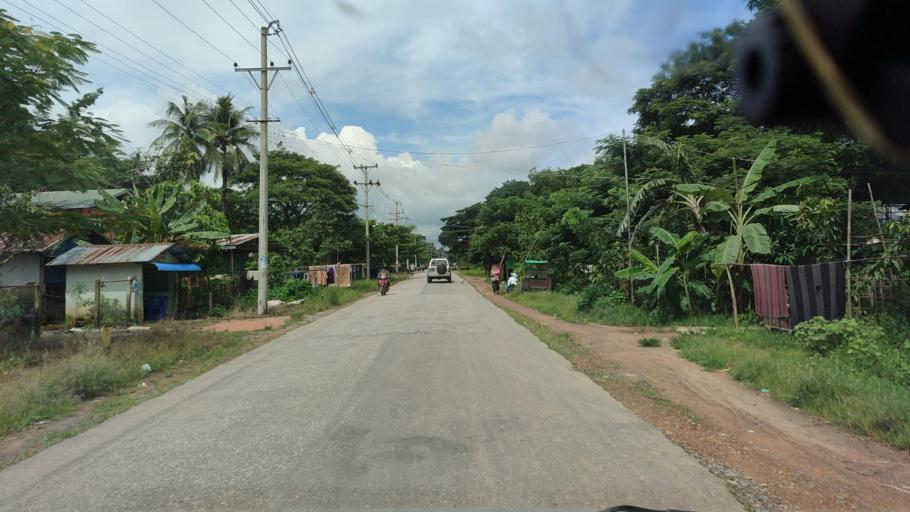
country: MM
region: Bago
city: Thanatpin
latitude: 17.0922
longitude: 96.4694
